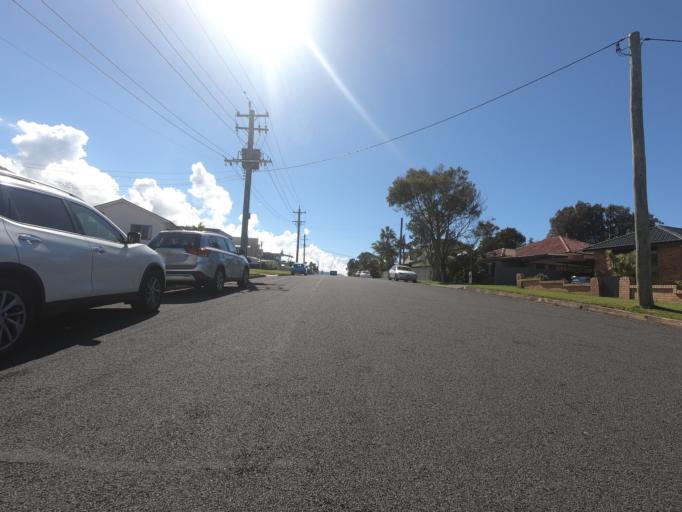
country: AU
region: New South Wales
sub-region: Wollongong
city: Bulli
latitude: -34.3314
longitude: 150.9244
